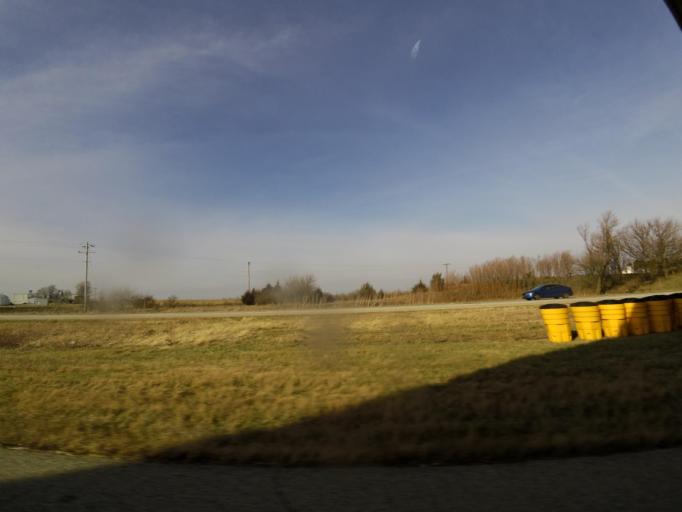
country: US
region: Illinois
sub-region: Macon County
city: Harristown
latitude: 39.8753
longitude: -89.0291
